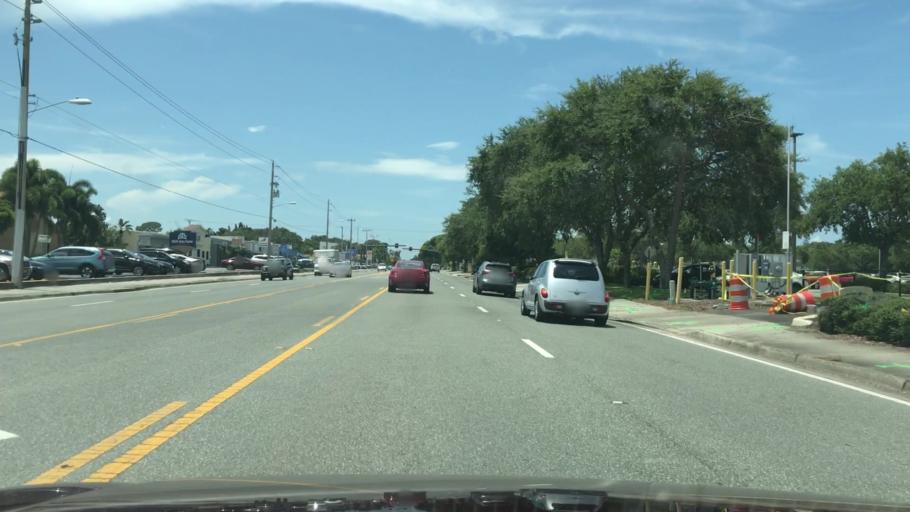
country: US
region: Florida
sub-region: Sarasota County
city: Southgate
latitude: 27.3013
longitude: -82.5142
